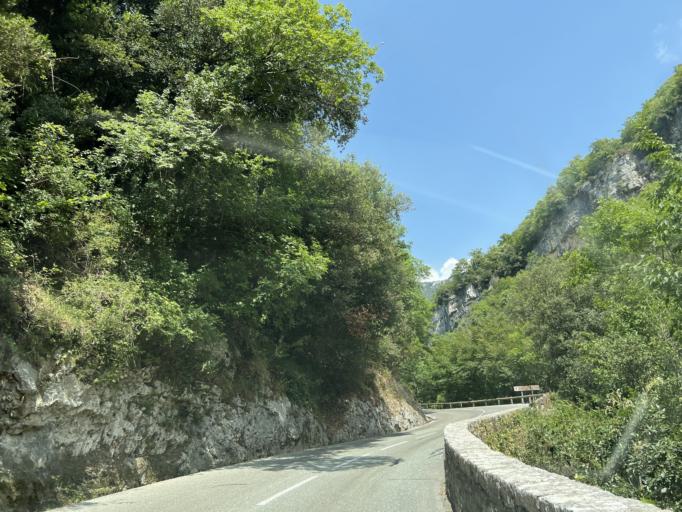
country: FR
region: Provence-Alpes-Cote d'Azur
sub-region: Departement des Alpes-Maritimes
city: Tourrettes-sur-Loup
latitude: 43.7436
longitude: 6.9990
